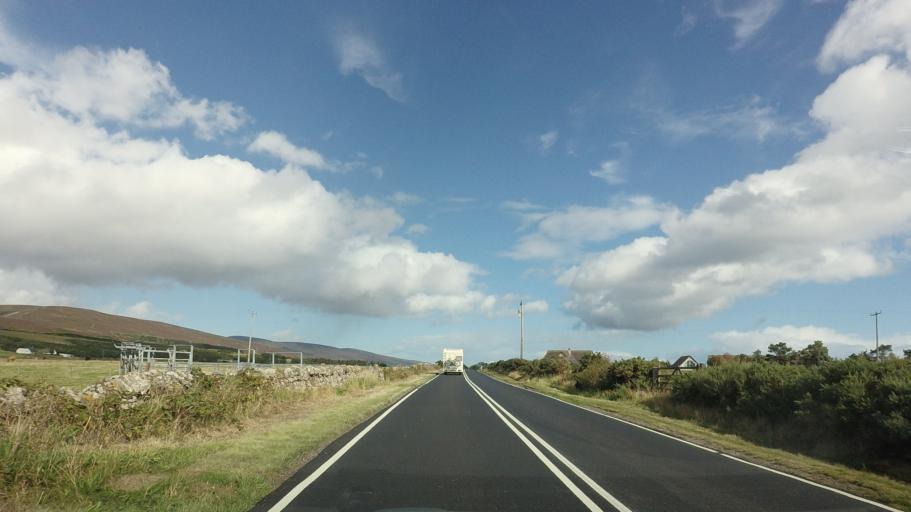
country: GB
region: Scotland
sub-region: Highland
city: Brora
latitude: 58.0291
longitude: -3.8515
